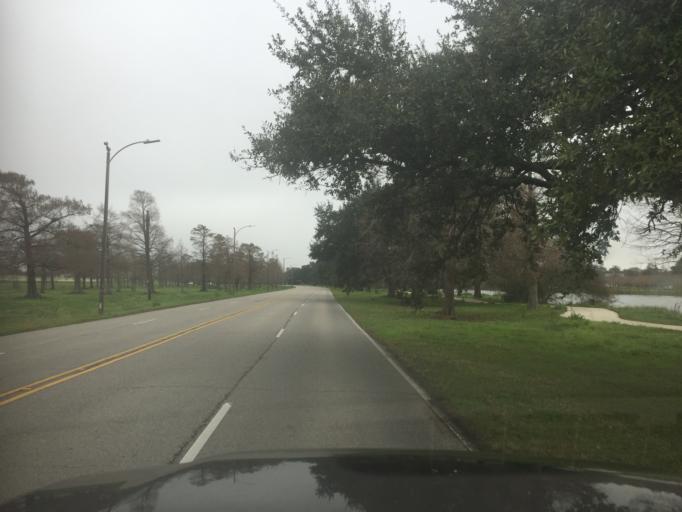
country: US
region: Louisiana
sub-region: Jefferson Parish
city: Metairie
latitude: 30.0146
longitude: -90.0975
